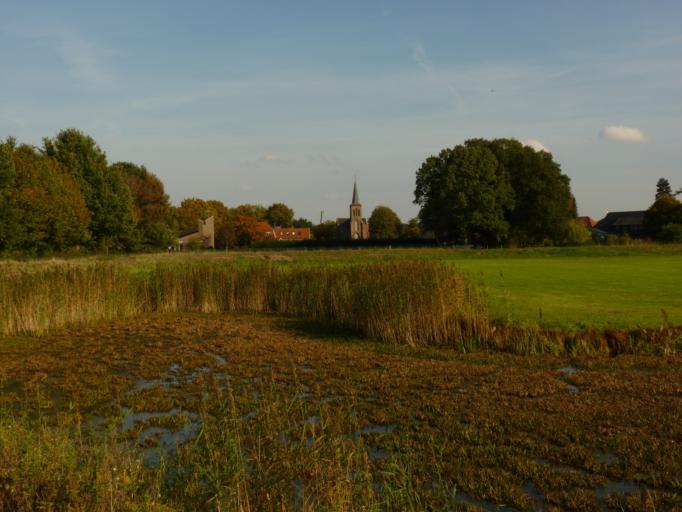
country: DE
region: Lower Saxony
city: Laar
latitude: 52.6134
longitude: 6.7374
